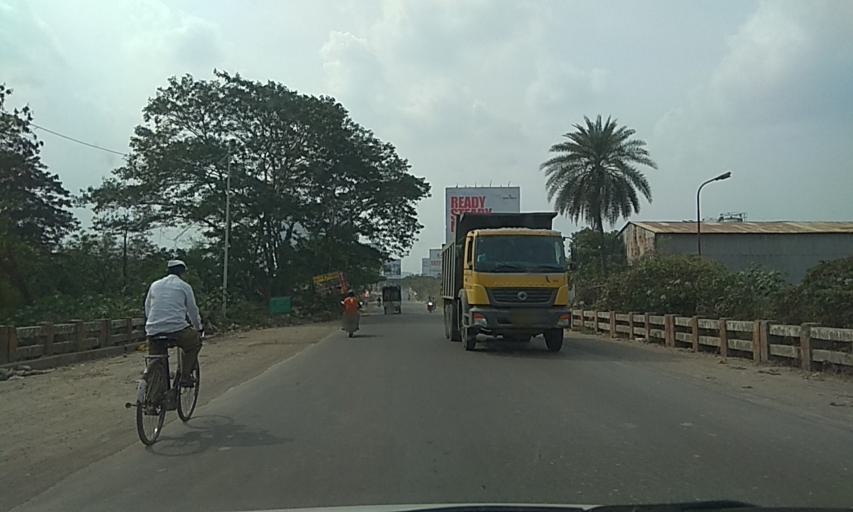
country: IN
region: Maharashtra
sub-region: Pune Division
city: Pimpri
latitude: 18.5817
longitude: 73.7248
